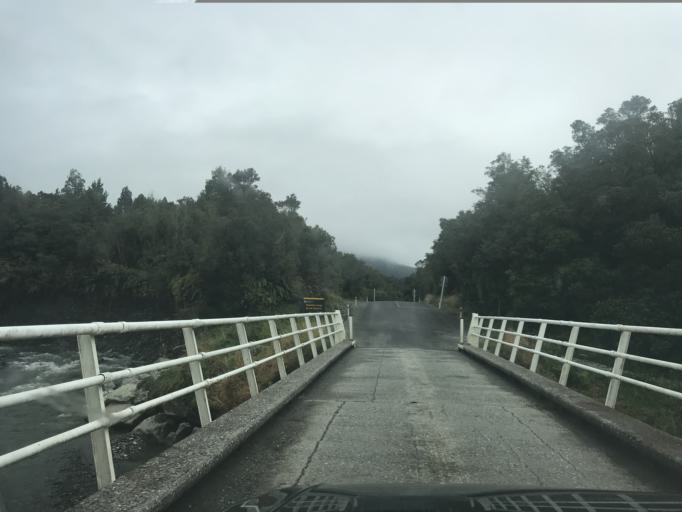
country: NZ
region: West Coast
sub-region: Westland District
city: Hokitika
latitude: -42.9528
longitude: 171.0232
